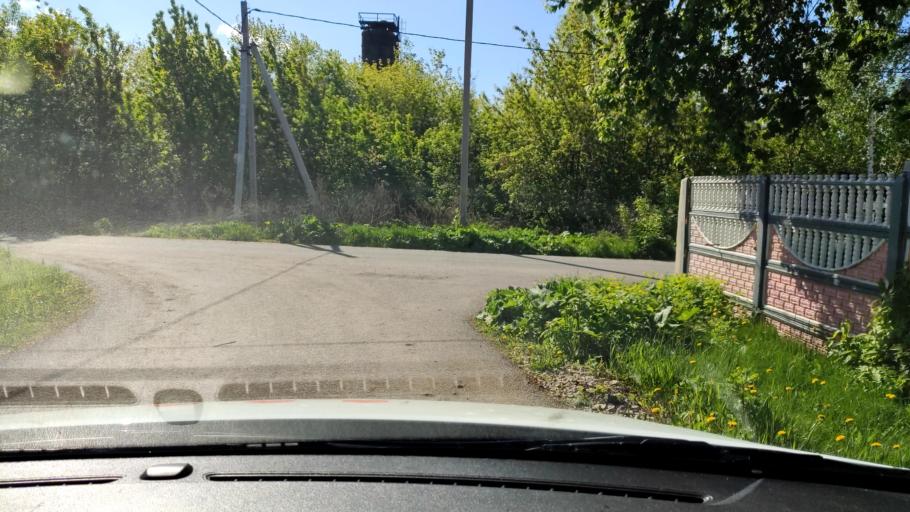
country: RU
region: Tatarstan
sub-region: Gorod Kazan'
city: Kazan
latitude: 55.7350
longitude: 49.0921
